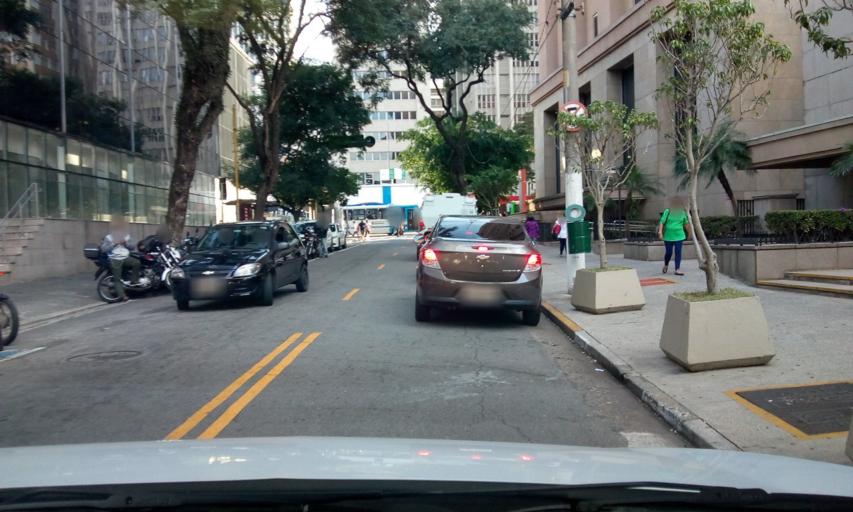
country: BR
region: Sao Paulo
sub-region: Sao Paulo
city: Sao Paulo
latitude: -23.5621
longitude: -46.6545
